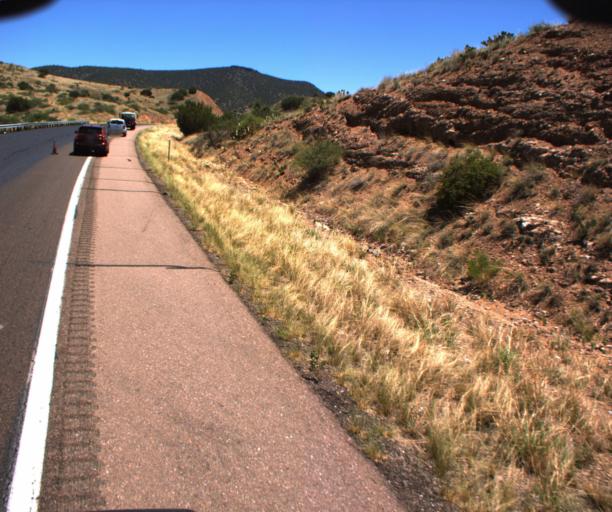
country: US
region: Arizona
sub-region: Gila County
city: Payson
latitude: 34.1385
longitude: -111.3290
